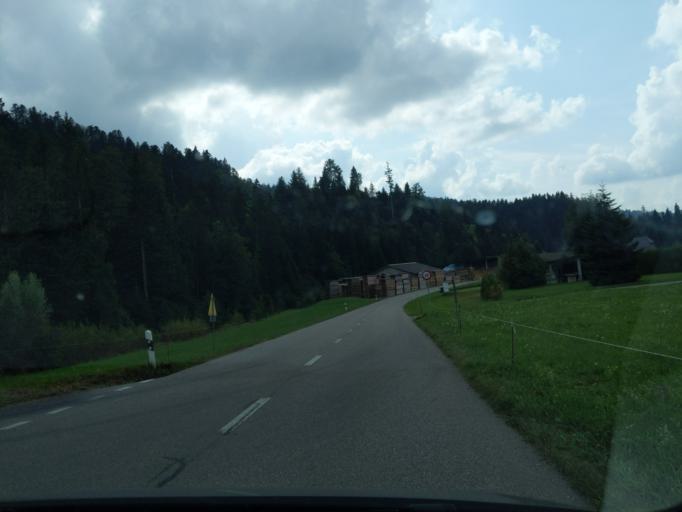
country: CH
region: Bern
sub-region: Oberaargau
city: Wyssachen
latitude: 47.0481
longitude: 7.8248
